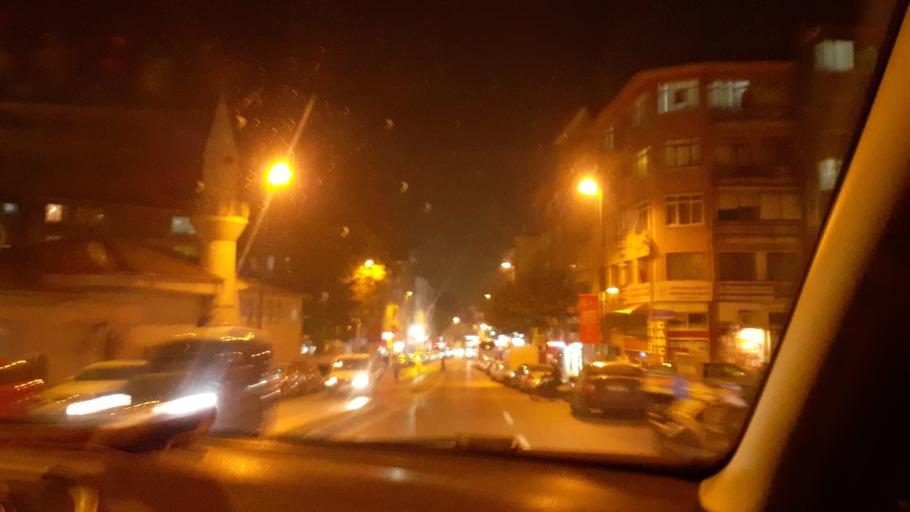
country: TR
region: Istanbul
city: UEskuedar
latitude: 41.0266
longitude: 29.0231
